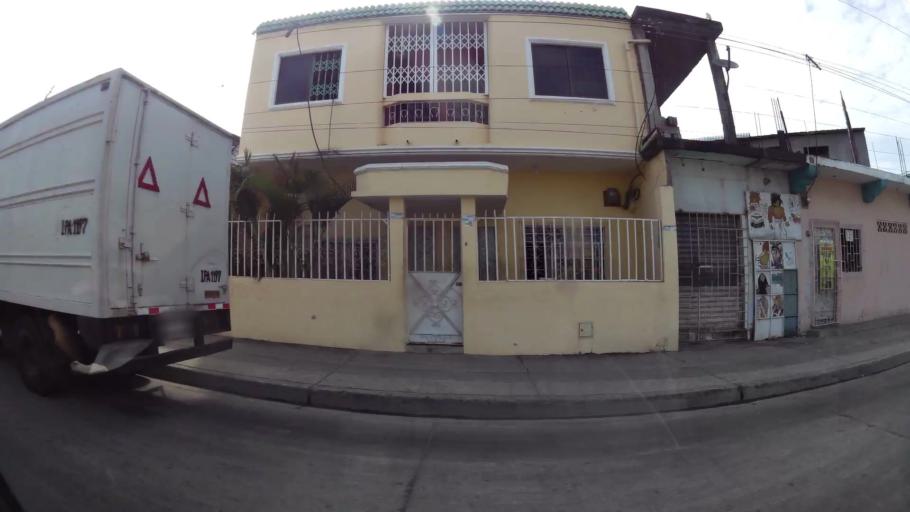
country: EC
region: Guayas
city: Guayaquil
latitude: -2.2582
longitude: -79.8790
